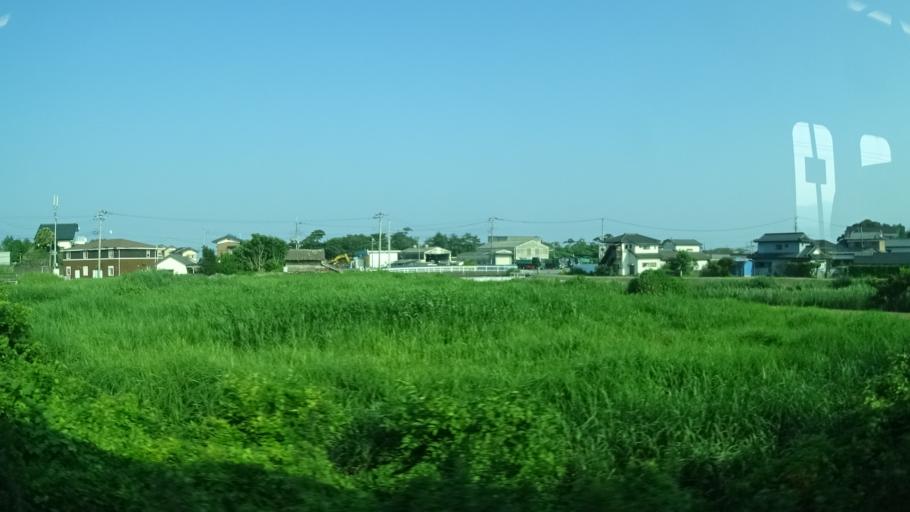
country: JP
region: Ibaraki
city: Kitaibaraki
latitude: 36.7584
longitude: 140.7336
